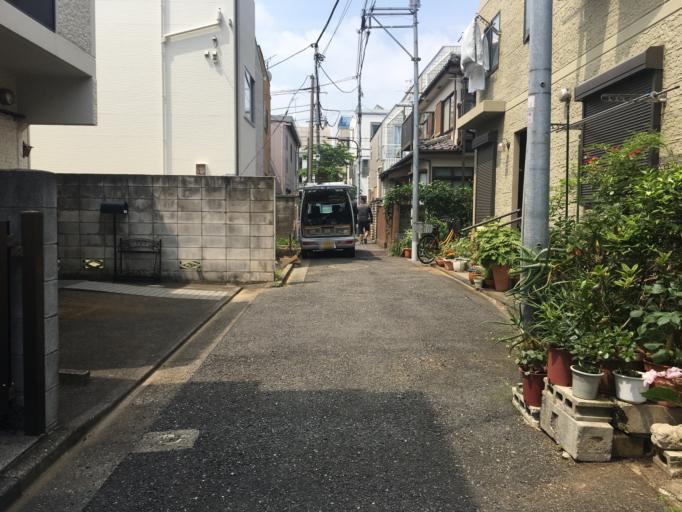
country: JP
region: Tokyo
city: Tokyo
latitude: 35.7295
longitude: 139.6939
